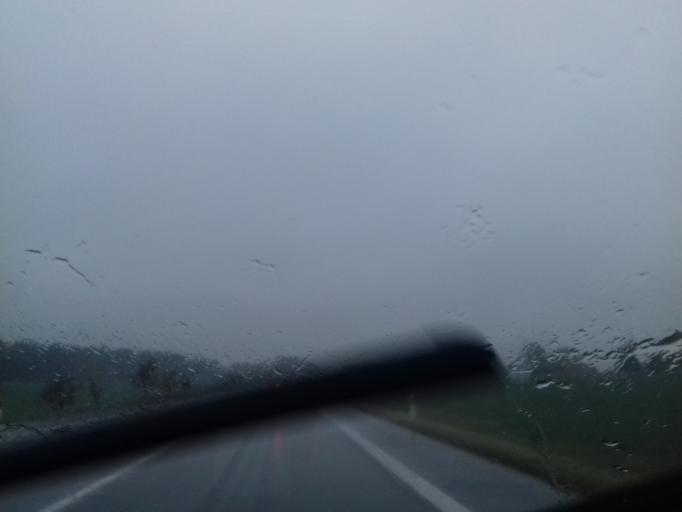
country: CZ
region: Pardubicky
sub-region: Okres Svitavy
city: Svitavy
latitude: 49.8184
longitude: 16.4099
